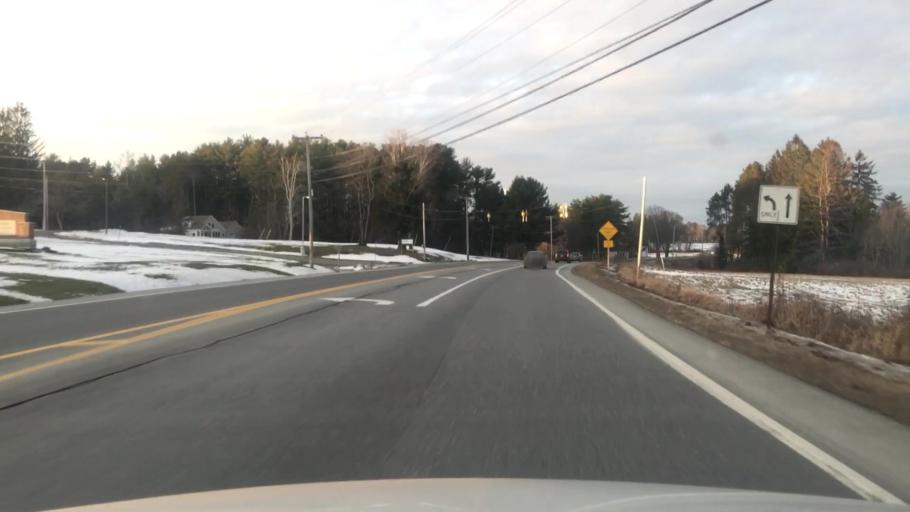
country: US
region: Maine
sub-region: Somerset County
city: Fairfield
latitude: 44.6696
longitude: -69.6303
